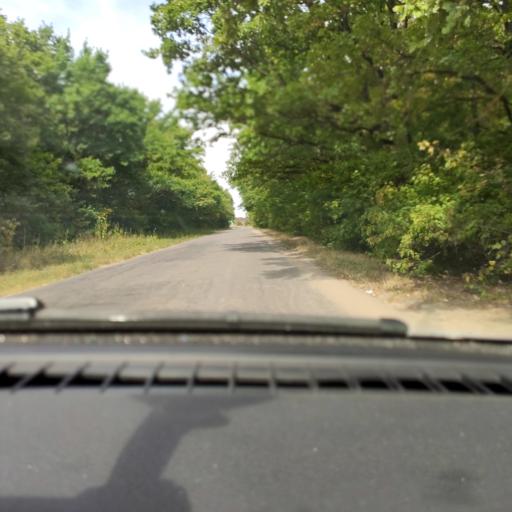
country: RU
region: Voronezj
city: Pridonskoy
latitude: 51.7387
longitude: 39.0553
